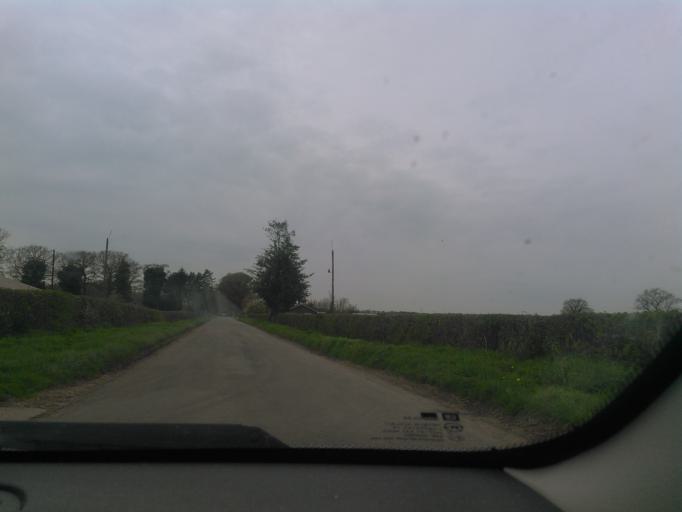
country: GB
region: England
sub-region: Shropshire
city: Shawbury
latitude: 52.8026
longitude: -2.5983
